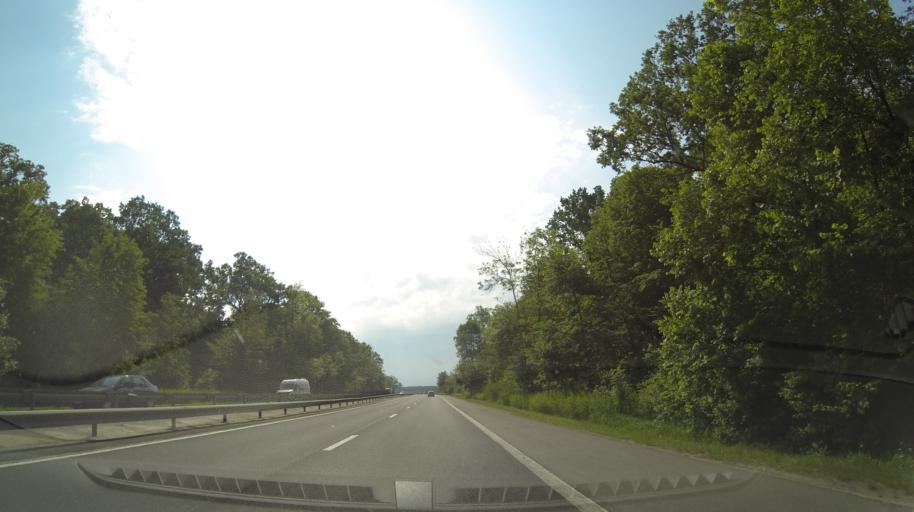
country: RO
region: Giurgiu
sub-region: Comuna Vanatorii Mici
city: Vanatorii Mici
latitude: 44.4994
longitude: 25.5857
